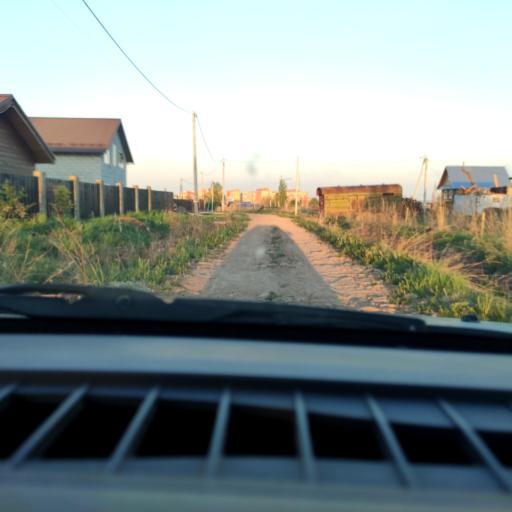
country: RU
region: Perm
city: Froly
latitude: 57.9289
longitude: 56.2880
